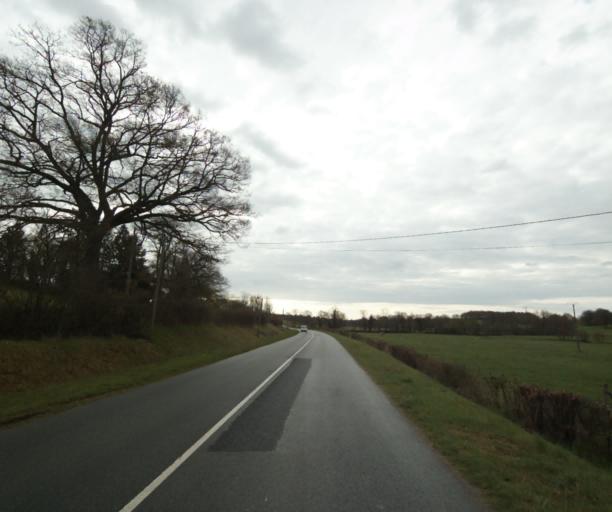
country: FR
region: Auvergne
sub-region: Departement de l'Allier
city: Toulon-sur-Allier
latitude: 46.4972
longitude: 3.3867
